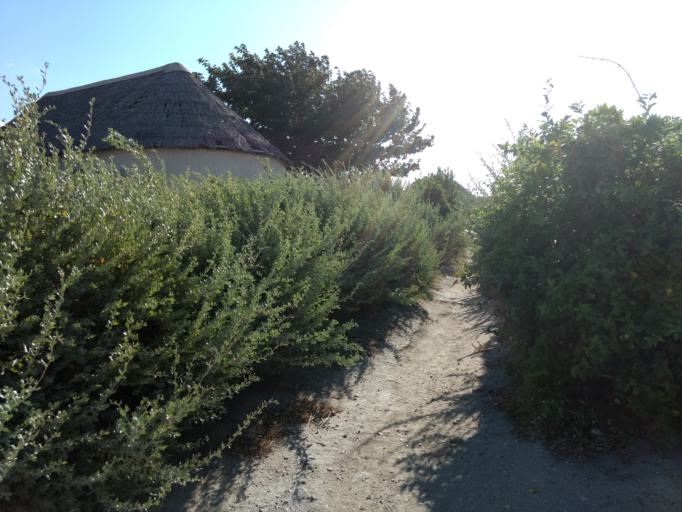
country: FR
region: Languedoc-Roussillon
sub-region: Departement des Pyrenees-Orientales
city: Le Barcares
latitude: 42.8225
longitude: 3.0264
